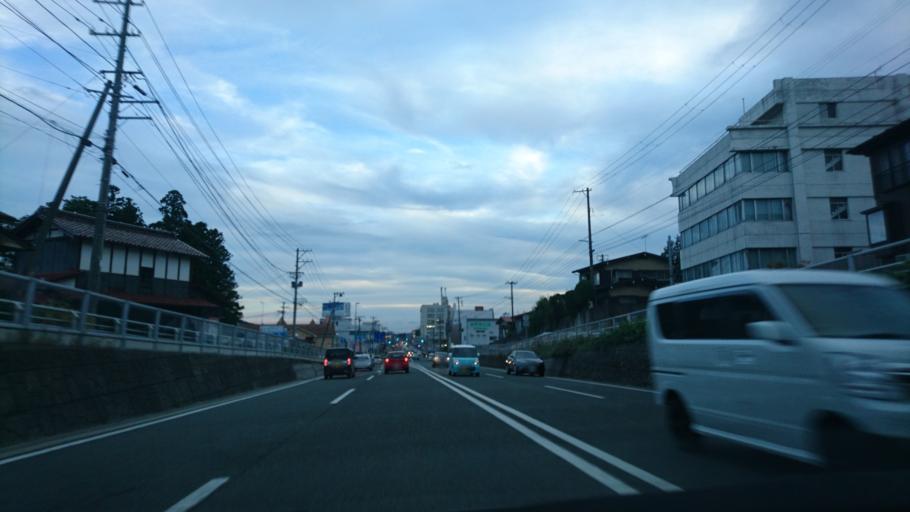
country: JP
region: Iwate
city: Morioka-shi
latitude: 39.6972
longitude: 141.1679
